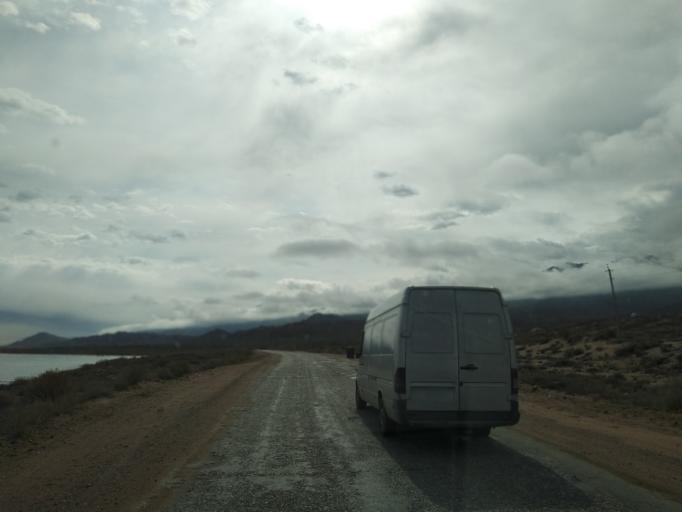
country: KG
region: Ysyk-Koel
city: Kadzhi-Say
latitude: 42.1551
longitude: 77.0832
